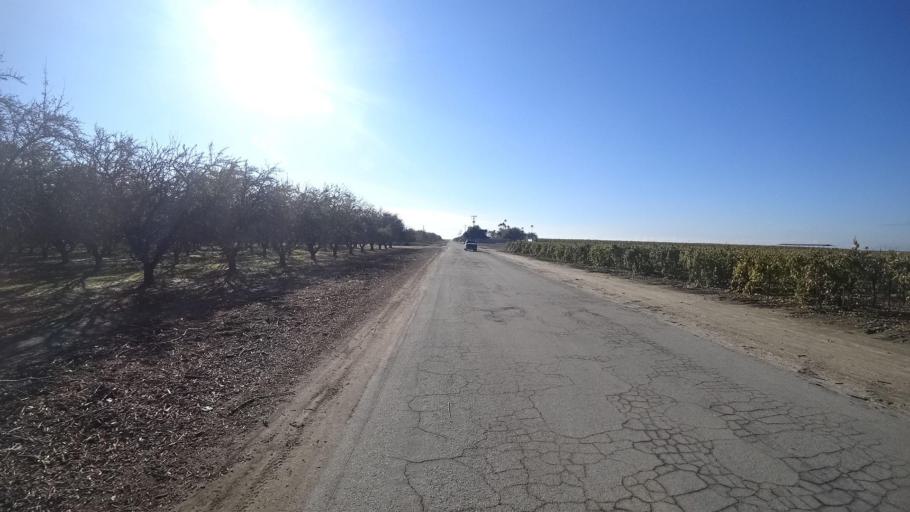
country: US
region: California
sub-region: Kern County
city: McFarland
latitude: 35.6859
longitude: -119.2675
